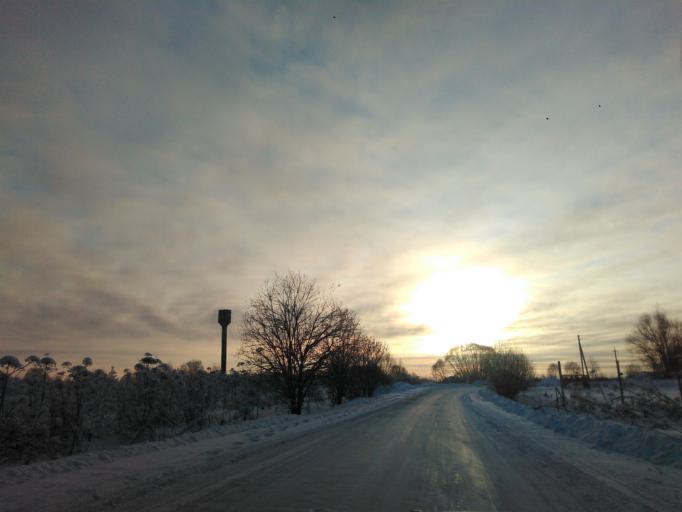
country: RU
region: Tverskaya
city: Zavidovo
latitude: 56.6317
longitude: 36.6178
